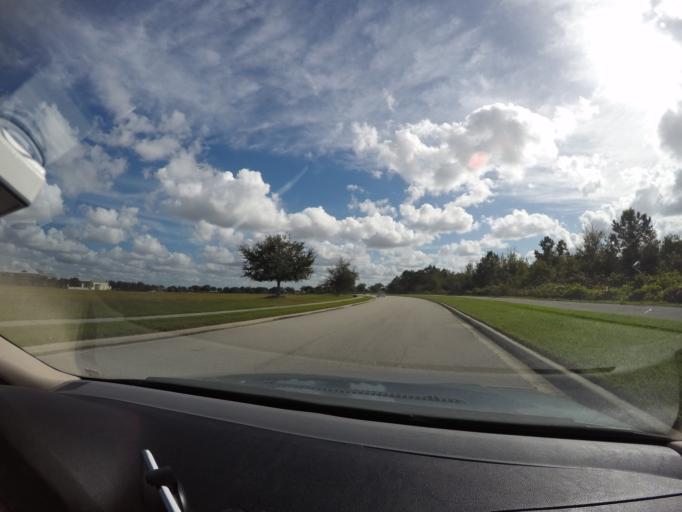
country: US
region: Florida
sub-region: Orange County
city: Wedgefield
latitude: 28.4128
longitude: -81.2059
